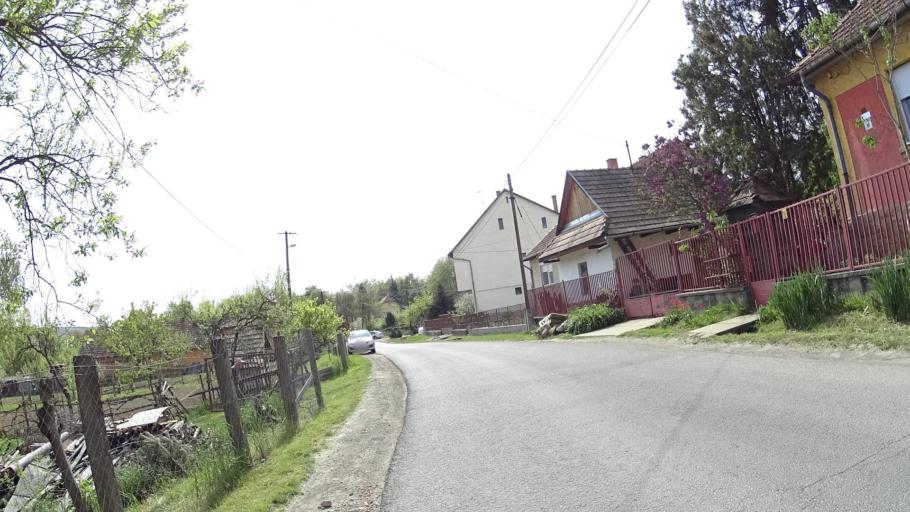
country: HU
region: Nograd
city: Romhany
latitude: 47.9398
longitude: 19.2885
